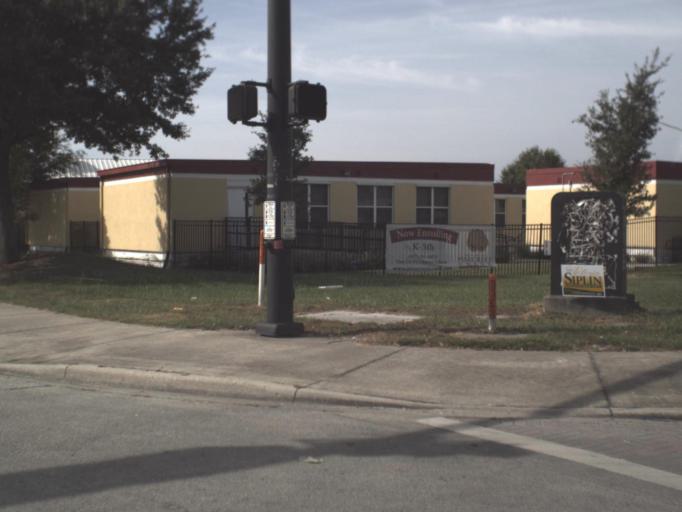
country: US
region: Florida
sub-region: Orange County
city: Orlando
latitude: 28.5289
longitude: -81.4145
